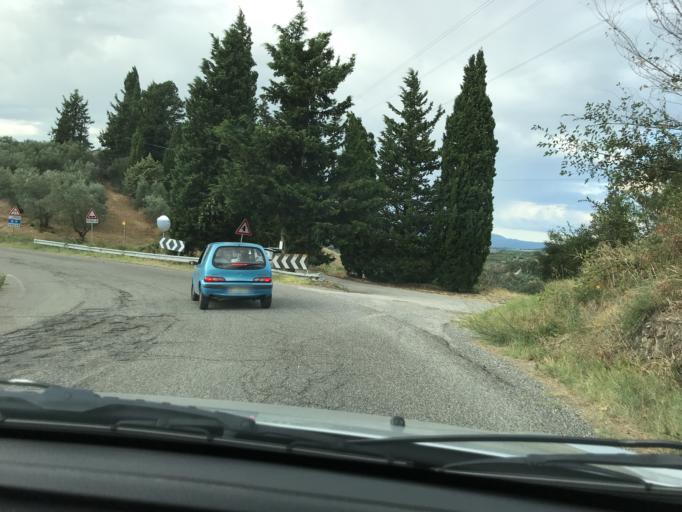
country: IT
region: Umbria
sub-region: Provincia di Terni
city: Montecchio
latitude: 42.6484
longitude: 12.2797
